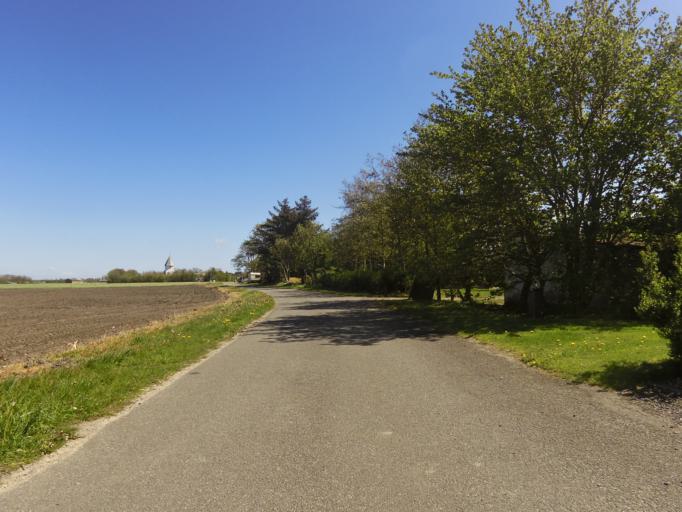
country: DK
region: South Denmark
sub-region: Tonder Kommune
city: Sherrebek
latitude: 55.2381
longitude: 8.7080
